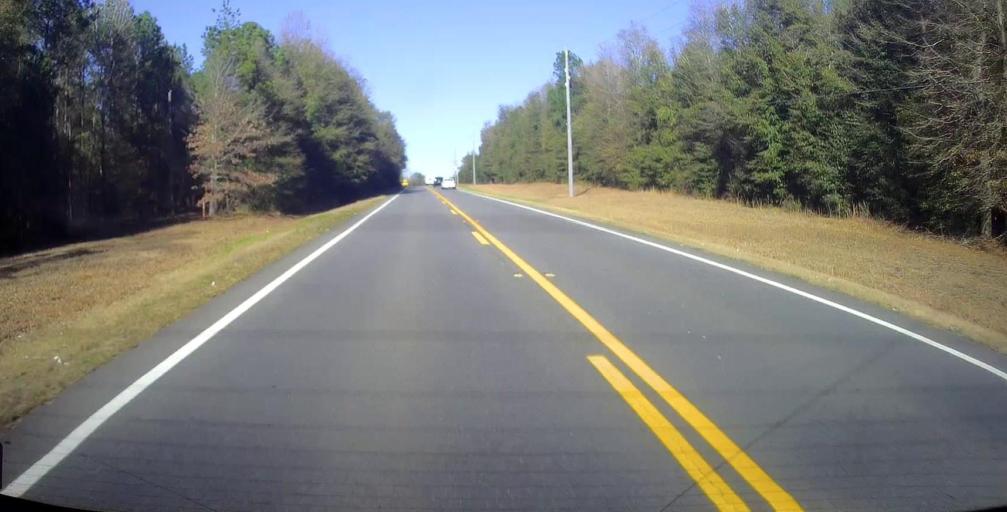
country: US
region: Georgia
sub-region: Macon County
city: Oglethorpe
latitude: 32.2348
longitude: -84.0958
